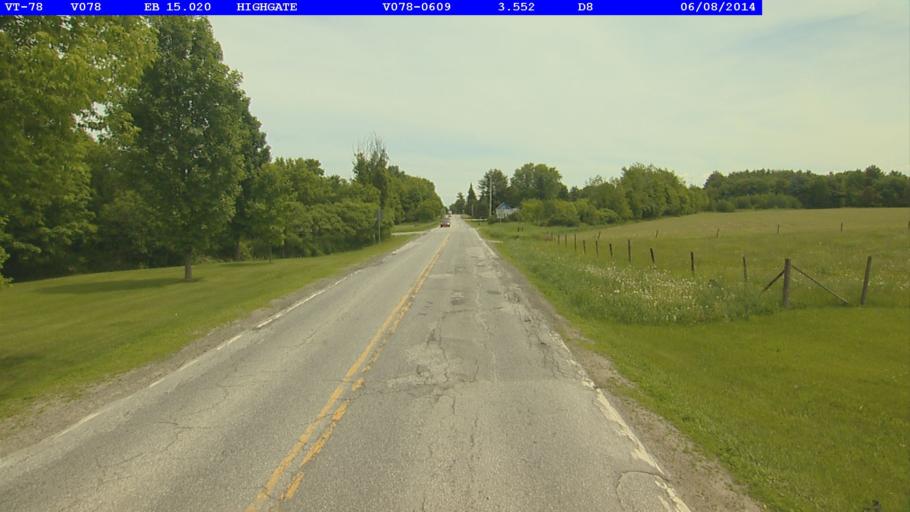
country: US
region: Vermont
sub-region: Franklin County
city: Swanton
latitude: 44.9409
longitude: -73.0360
